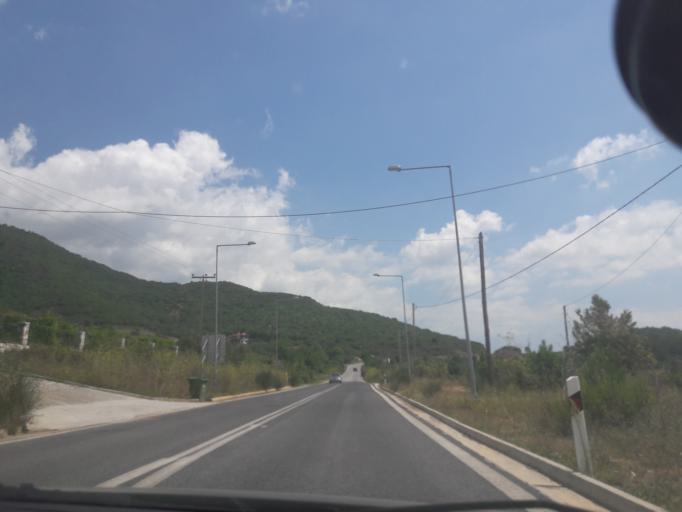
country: GR
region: Central Macedonia
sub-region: Nomos Chalkidikis
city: Polygyros
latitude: 40.3728
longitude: 23.4554
